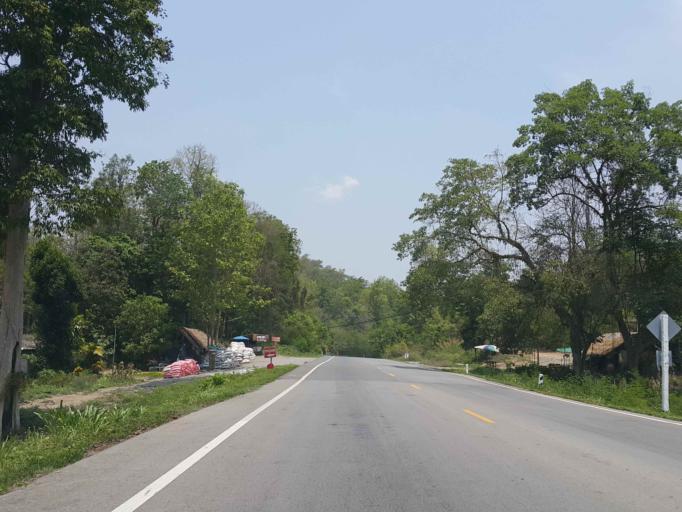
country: TH
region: Chiang Mai
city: Mae On
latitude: 18.9466
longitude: 99.2338
